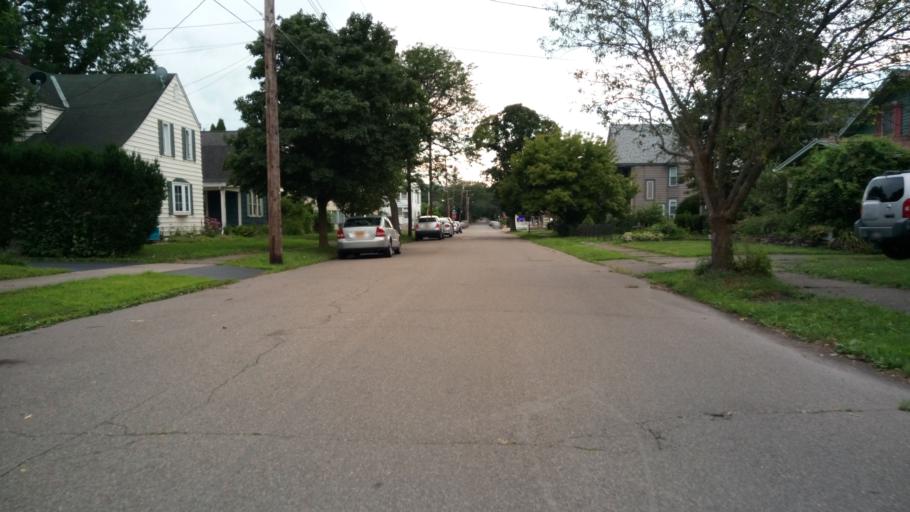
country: US
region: New York
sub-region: Chemung County
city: Elmira
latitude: 42.0852
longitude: -76.8207
